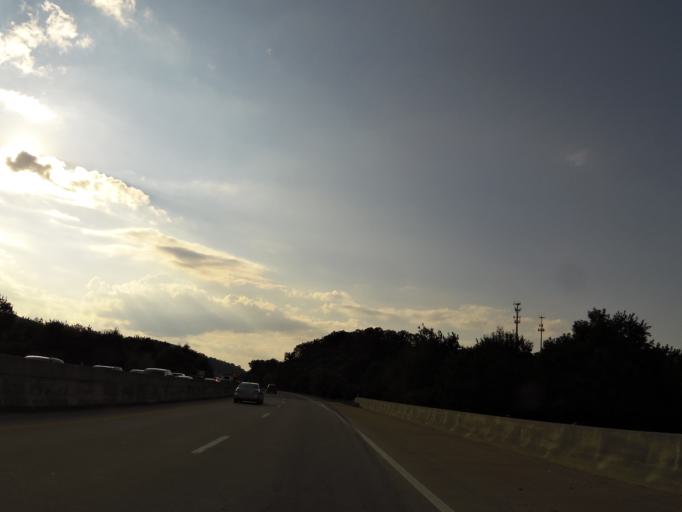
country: US
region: Tennessee
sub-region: Knox County
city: Farragut
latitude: 35.8848
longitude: -84.1020
